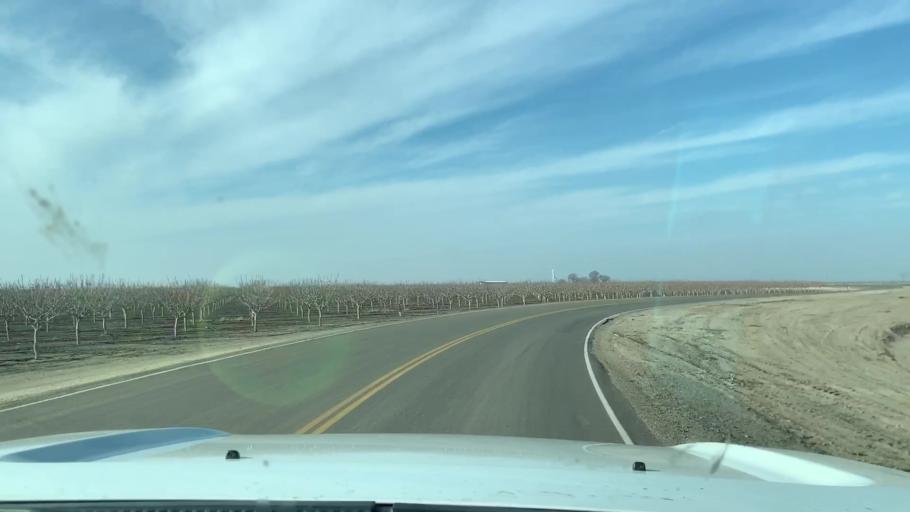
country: US
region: California
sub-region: Kern County
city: Buttonwillow
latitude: 35.4499
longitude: -119.5611
